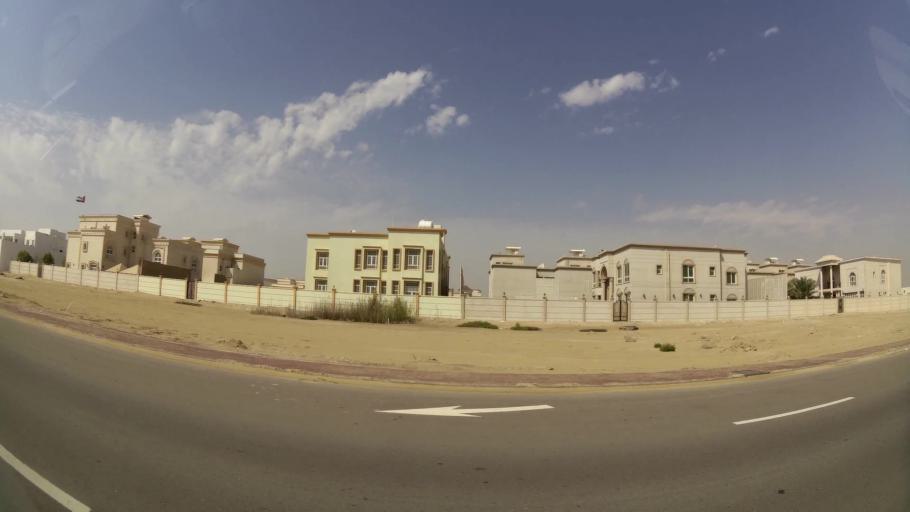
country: AE
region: Abu Dhabi
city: Abu Dhabi
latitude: 24.3048
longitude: 54.5639
